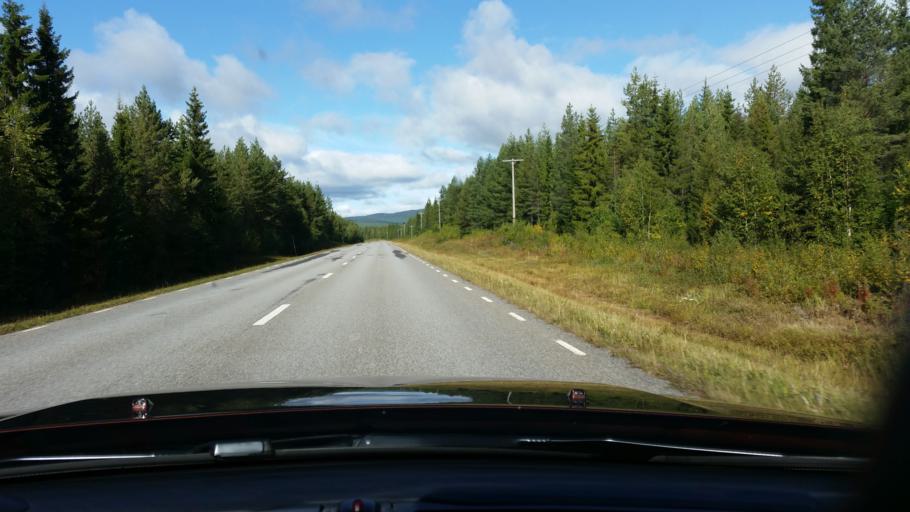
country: SE
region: Jaemtland
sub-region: Stroemsunds Kommun
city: Stroemsund
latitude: 64.2873
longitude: 15.3486
